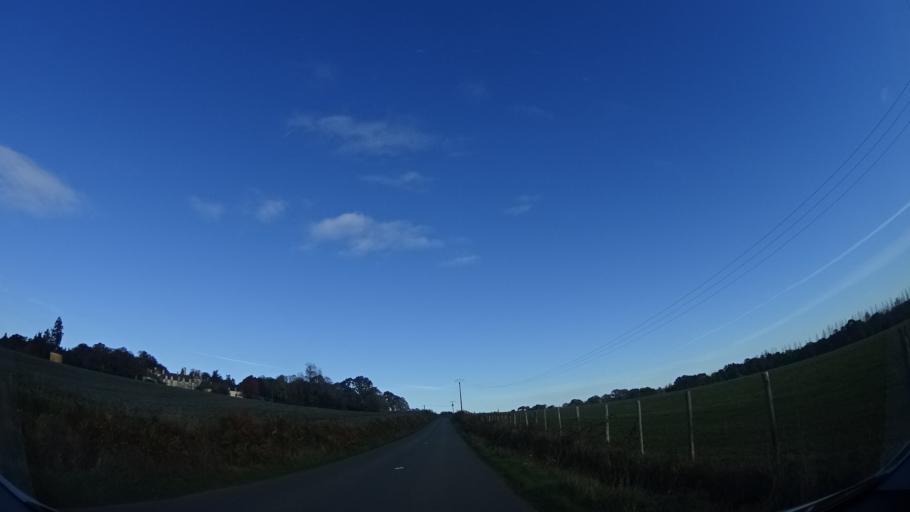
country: FR
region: Brittany
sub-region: Departement d'Ille-et-Vilaine
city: Geveze
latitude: 48.2087
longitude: -1.7911
